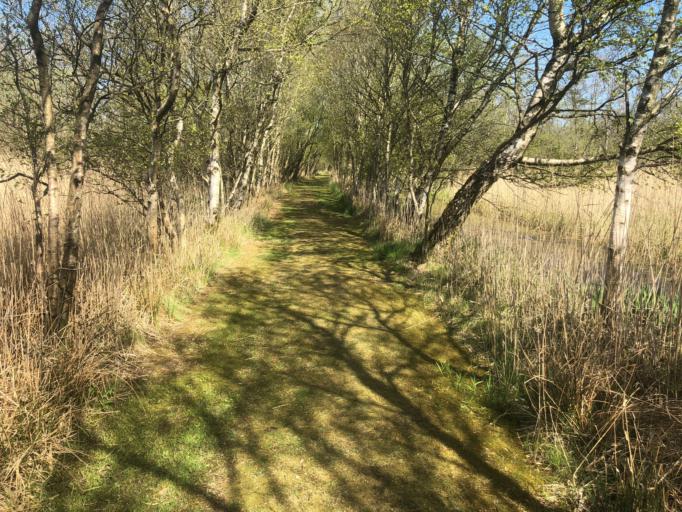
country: DK
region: Central Jutland
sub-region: Holstebro Kommune
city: Vinderup
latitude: 56.5694
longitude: 8.7914
